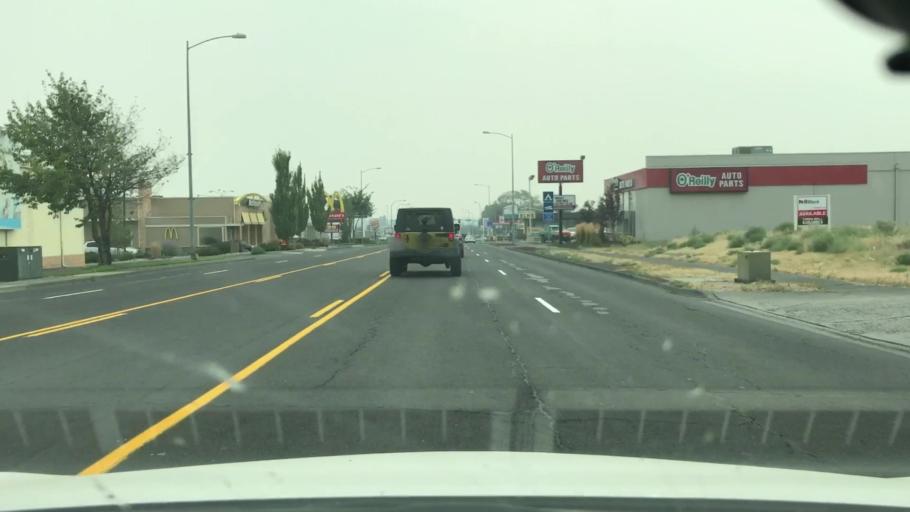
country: US
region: Washington
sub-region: Grant County
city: Moses Lake
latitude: 47.1408
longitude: -119.2784
